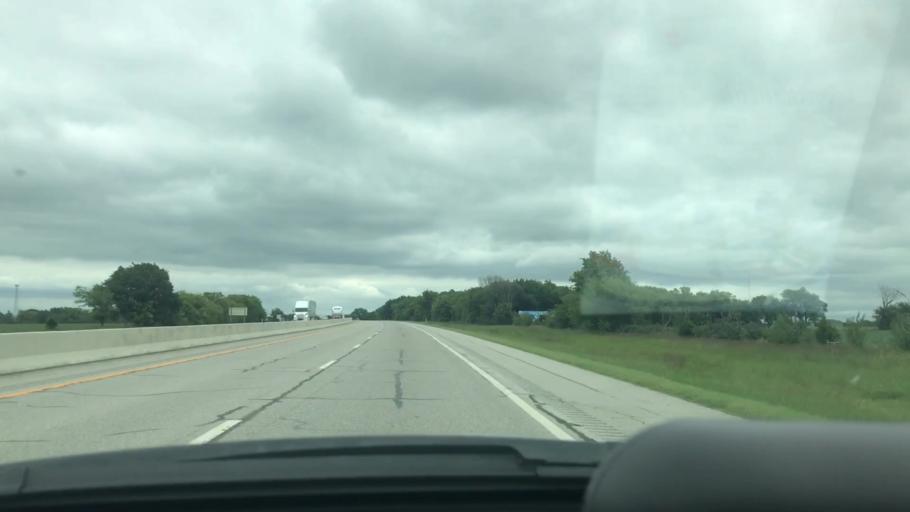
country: US
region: Oklahoma
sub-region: Ottawa County
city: Afton
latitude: 36.7342
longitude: -94.9128
